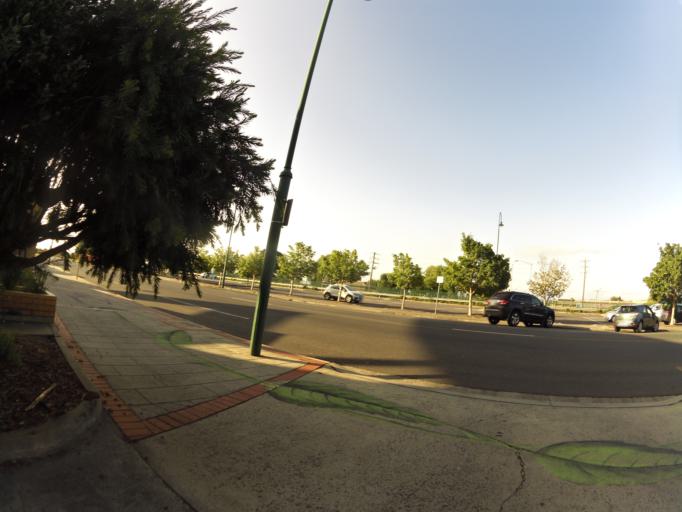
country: AU
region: Victoria
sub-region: Latrobe
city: Morwell
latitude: -38.2365
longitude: 146.3940
